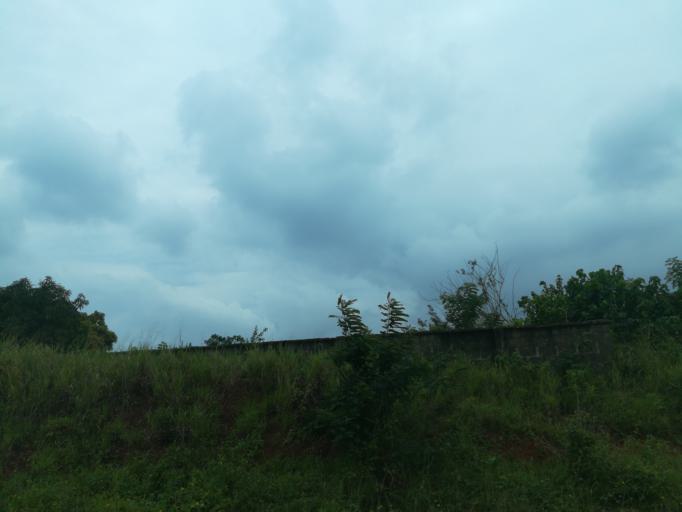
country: NG
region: Lagos
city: Ejirin
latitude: 6.6429
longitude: 3.7250
